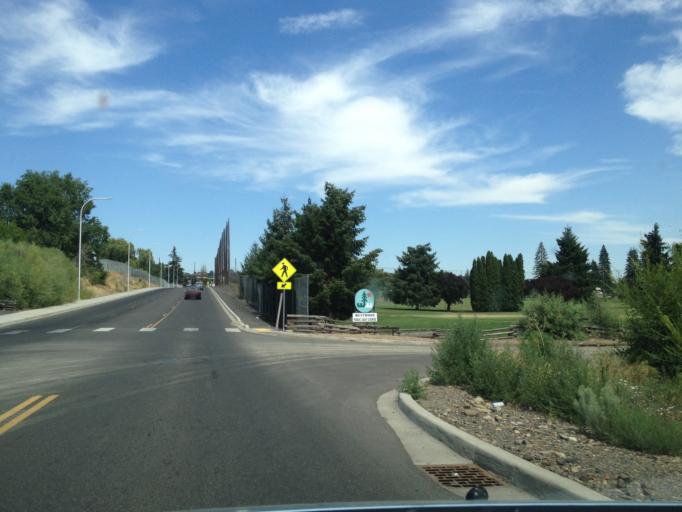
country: US
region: Washington
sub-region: Yakima County
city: West Valley
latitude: 46.5889
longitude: -120.5939
